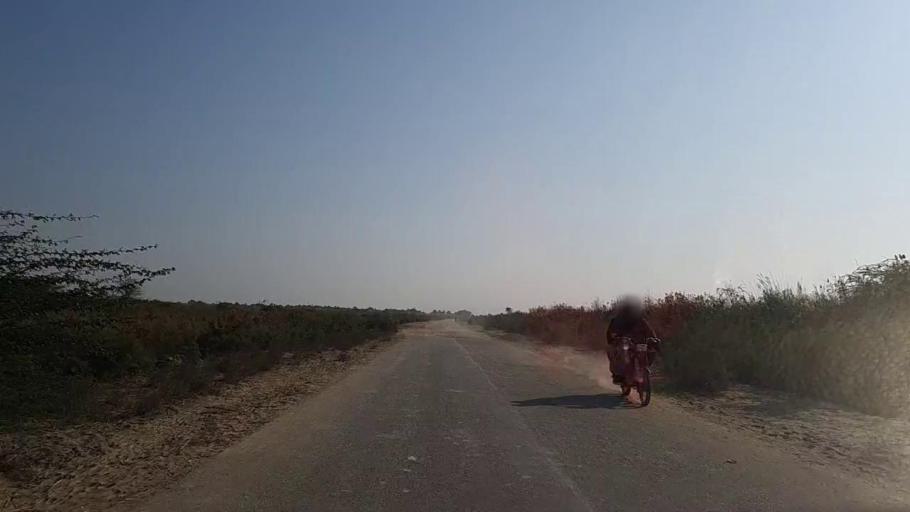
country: PK
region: Sindh
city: Tando Mittha Khan
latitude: 25.9088
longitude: 69.0764
